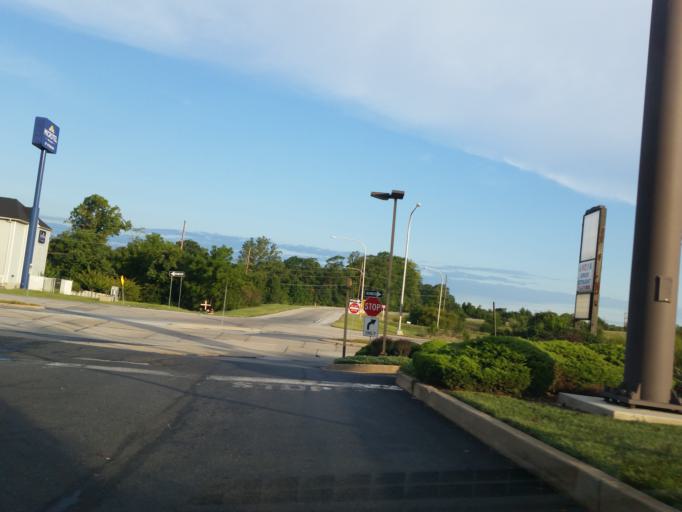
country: US
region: Delaware
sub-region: Kent County
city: Dover Base Housing
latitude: 39.1295
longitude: -75.4940
